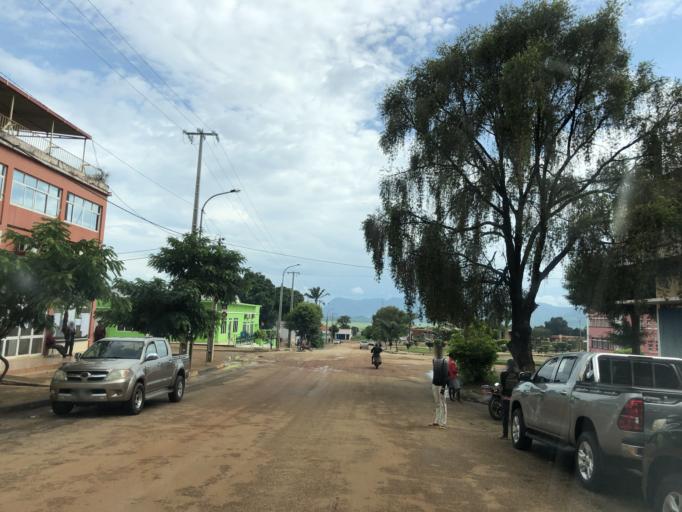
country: AO
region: Cuanza Sul
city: Uacu Cungo
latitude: -11.3640
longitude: 15.1179
